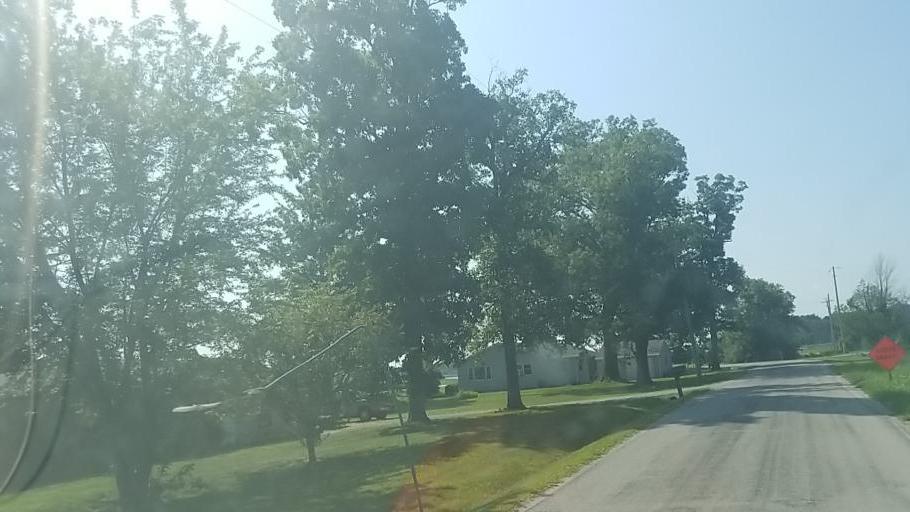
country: US
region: Ohio
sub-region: Marion County
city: Marion
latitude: 40.6947
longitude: -83.1498
